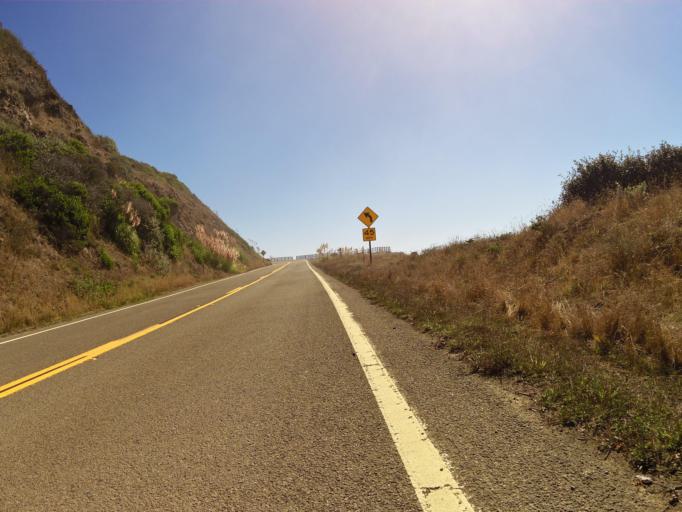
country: US
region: California
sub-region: Mendocino County
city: Fort Bragg
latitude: 39.7016
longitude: -123.8034
